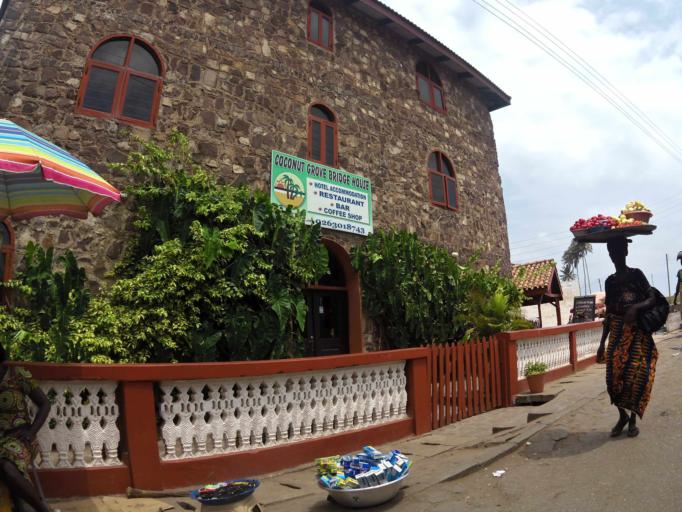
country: GH
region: Central
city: Elmina
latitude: 5.0836
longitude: -1.3493
